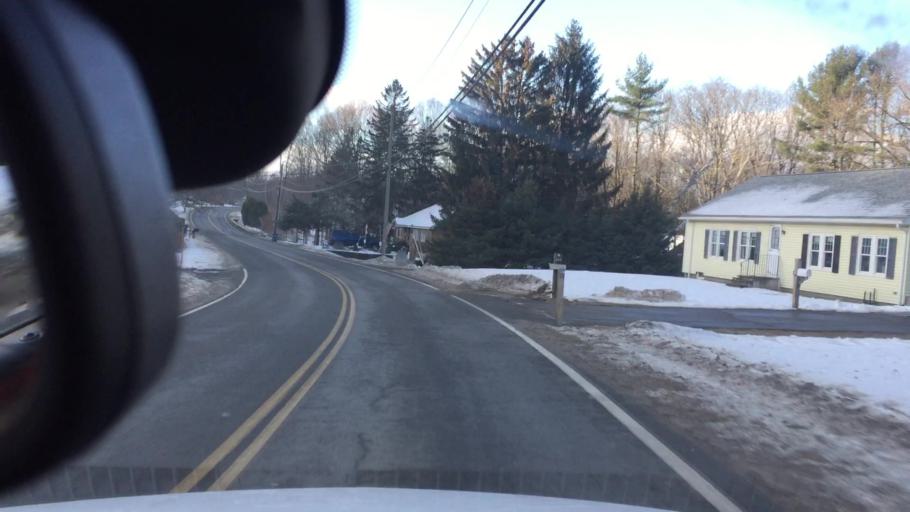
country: US
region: Massachusetts
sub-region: Franklin County
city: Montague
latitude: 42.5011
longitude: -72.5420
